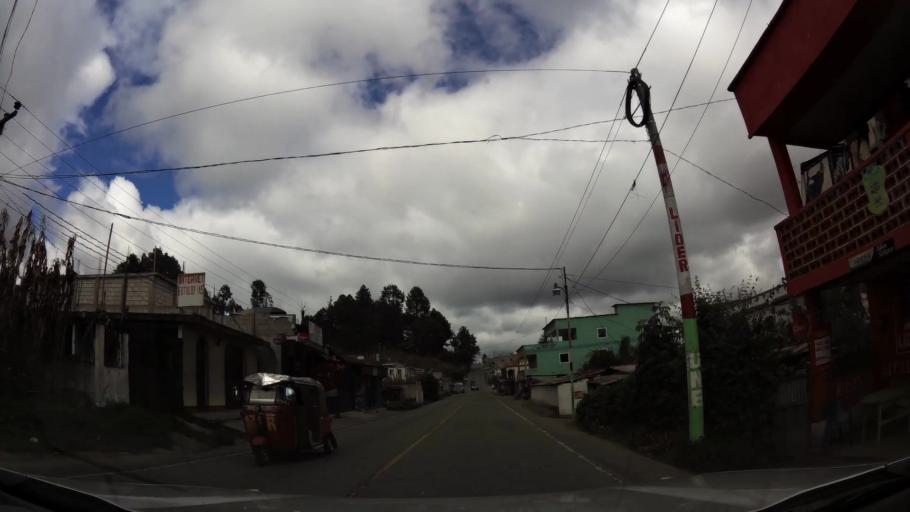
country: GT
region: Quiche
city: Chichicastenango
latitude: 14.8799
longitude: -91.1314
